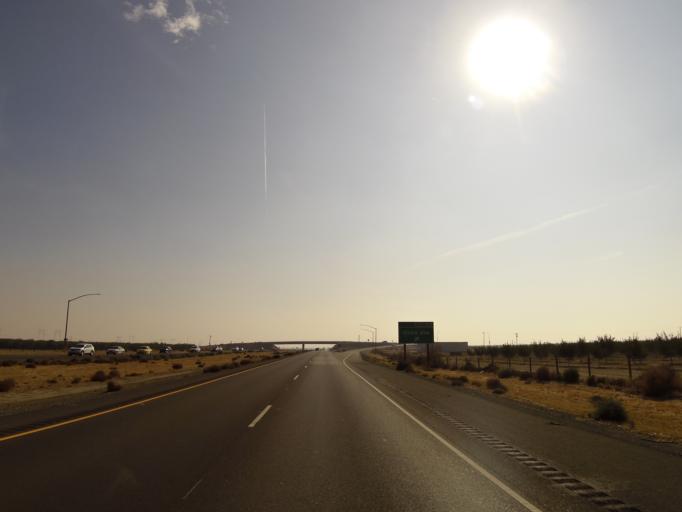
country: US
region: California
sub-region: Kings County
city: Kettleman City
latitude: 35.9376
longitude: -119.9154
